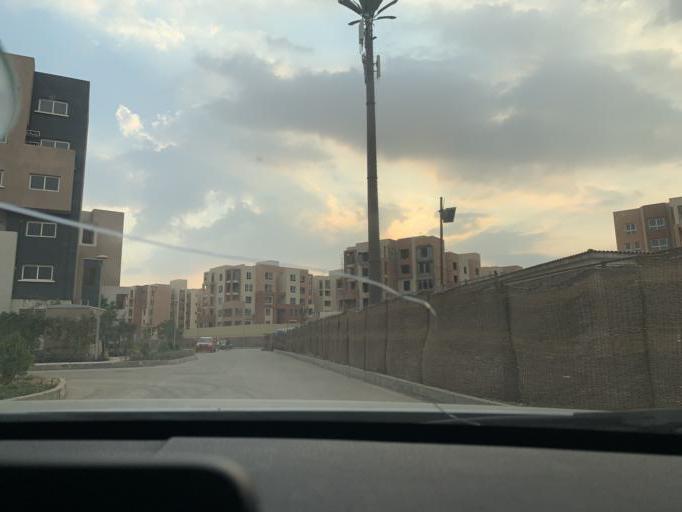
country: EG
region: Muhafazat al Qalyubiyah
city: Al Khankah
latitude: 30.0996
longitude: 31.6519
